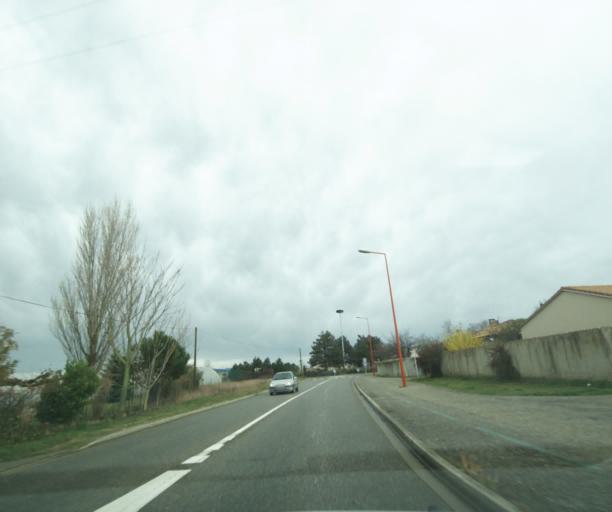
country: FR
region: Rhone-Alpes
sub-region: Departement de la Drome
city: Bourg-les-Valence
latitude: 44.9568
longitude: 4.9146
